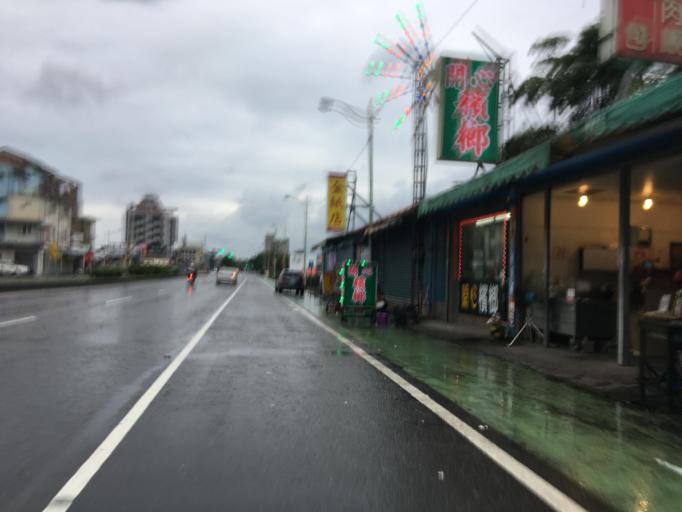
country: TW
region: Taiwan
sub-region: Yilan
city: Yilan
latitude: 24.6337
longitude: 121.7901
